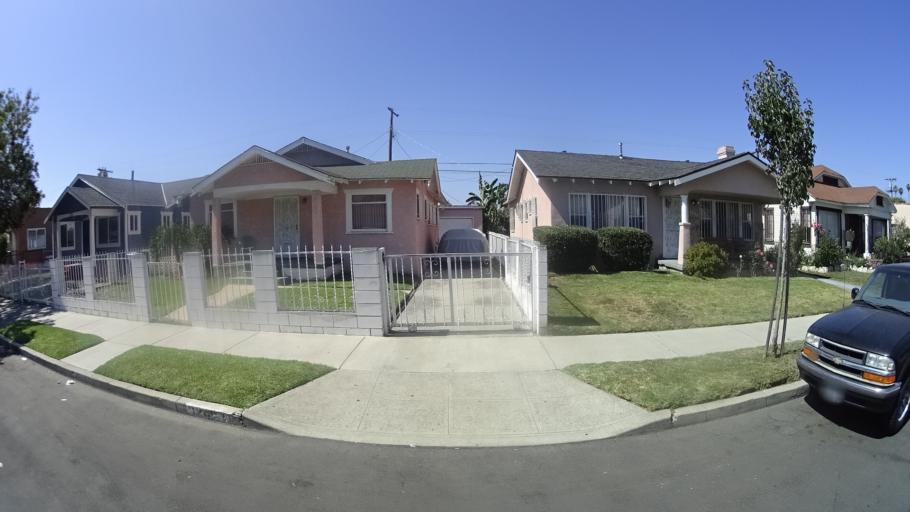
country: US
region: California
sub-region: Los Angeles County
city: Westmont
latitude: 33.9916
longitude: -118.2974
